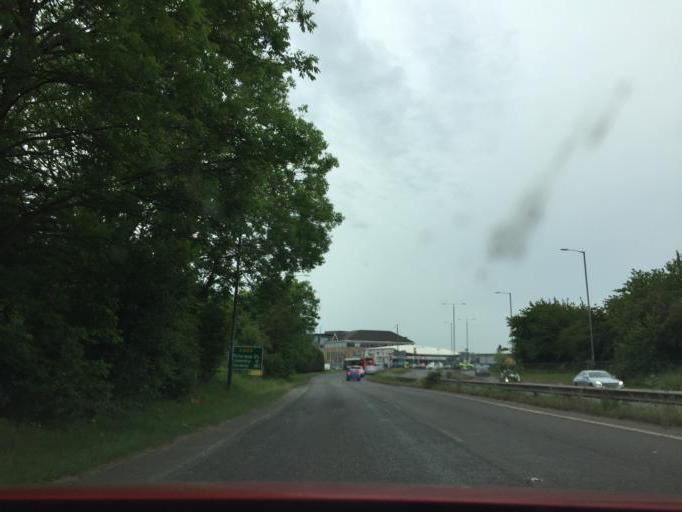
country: GB
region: England
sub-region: Warwickshire
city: Nuneaton
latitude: 52.5105
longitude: -1.4741
